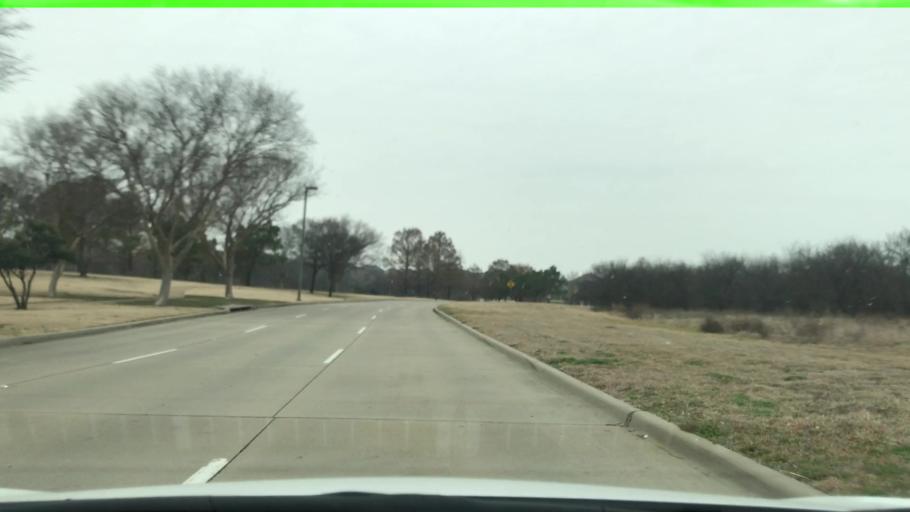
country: US
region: Texas
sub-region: Dallas County
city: Farmers Branch
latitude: 32.8933
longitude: -96.9499
